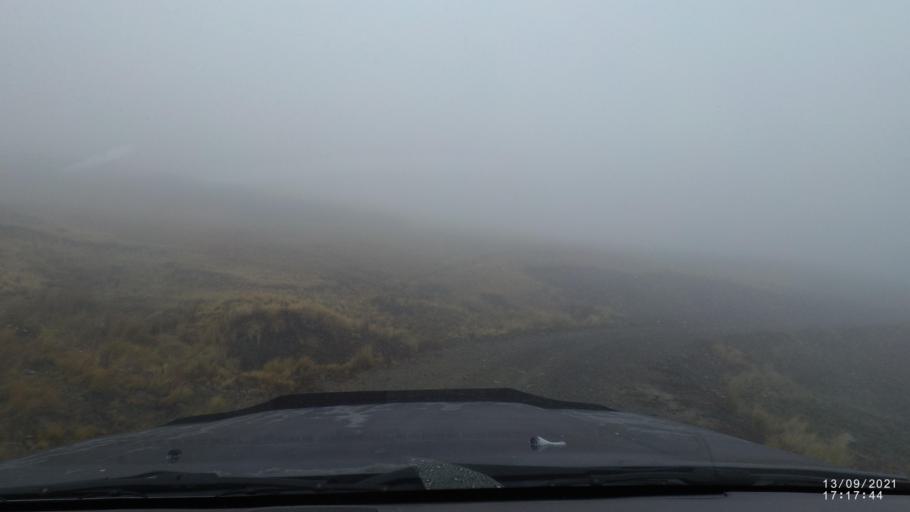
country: BO
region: Cochabamba
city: Colomi
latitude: -17.3463
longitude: -65.7598
